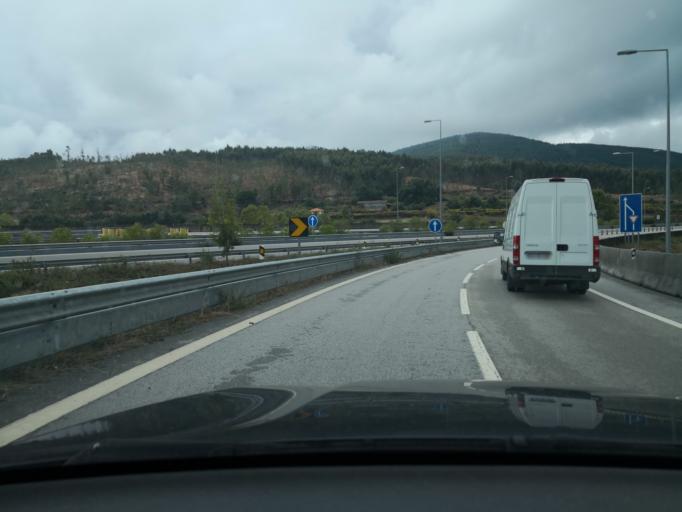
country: PT
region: Porto
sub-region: Lousada
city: Lousada
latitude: 41.2948
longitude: -8.2645
